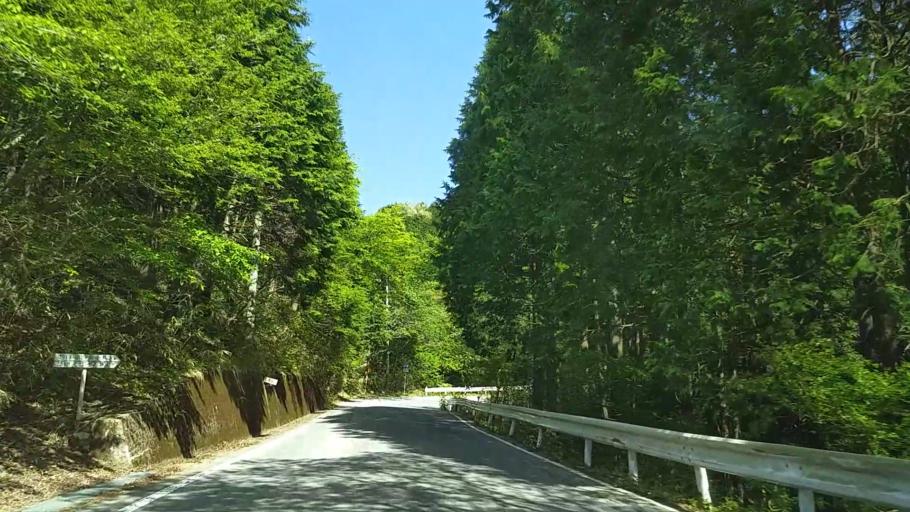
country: JP
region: Shizuoka
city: Gotemba
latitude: 35.2696
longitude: 138.9621
